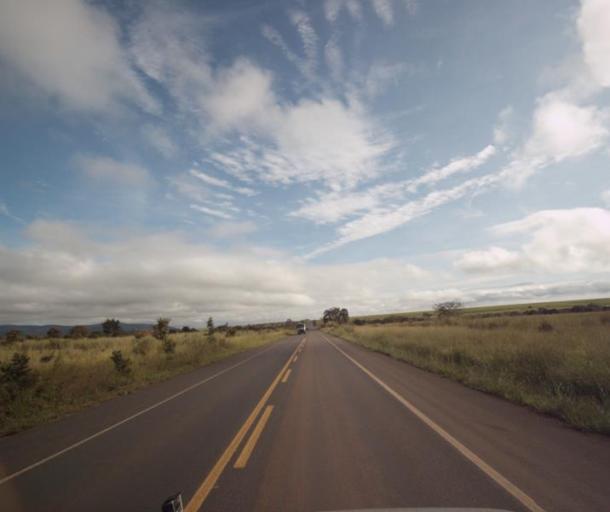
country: BR
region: Goias
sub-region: Padre Bernardo
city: Padre Bernardo
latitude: -15.4416
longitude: -48.6185
